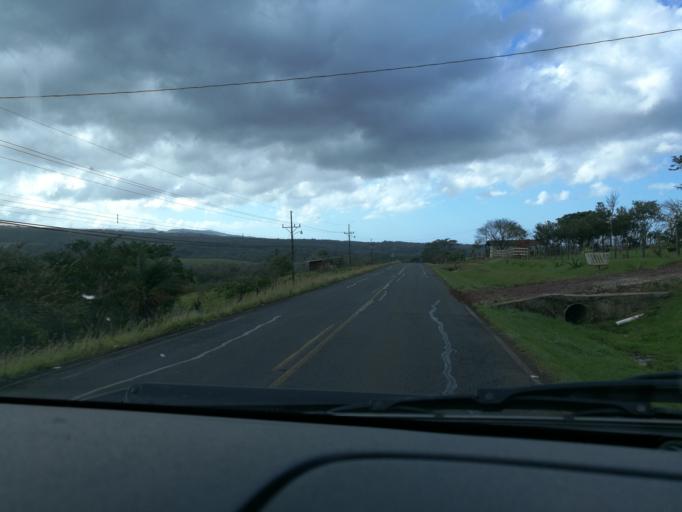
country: CR
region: Alajuela
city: Bijagua
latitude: 10.6698
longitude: -85.0902
